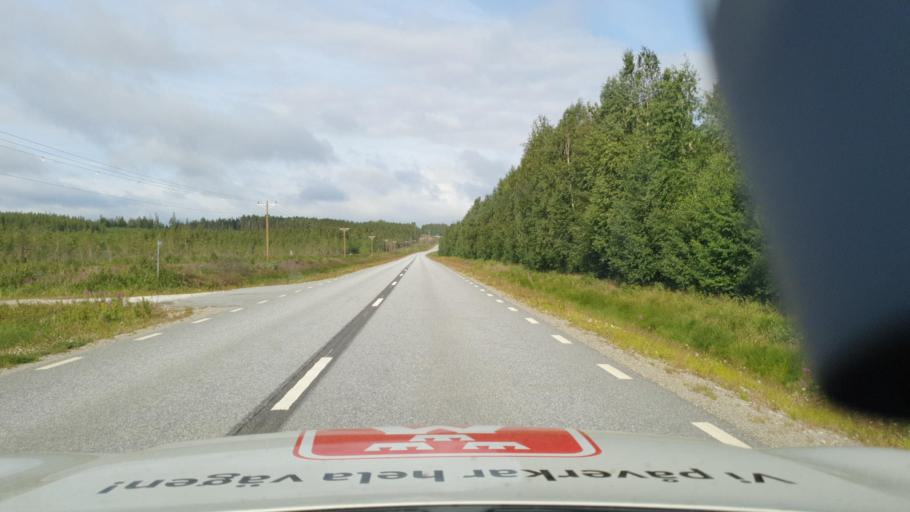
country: SE
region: Vaesterbotten
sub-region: Asele Kommun
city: Insjon
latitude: 64.1998
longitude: 17.5415
